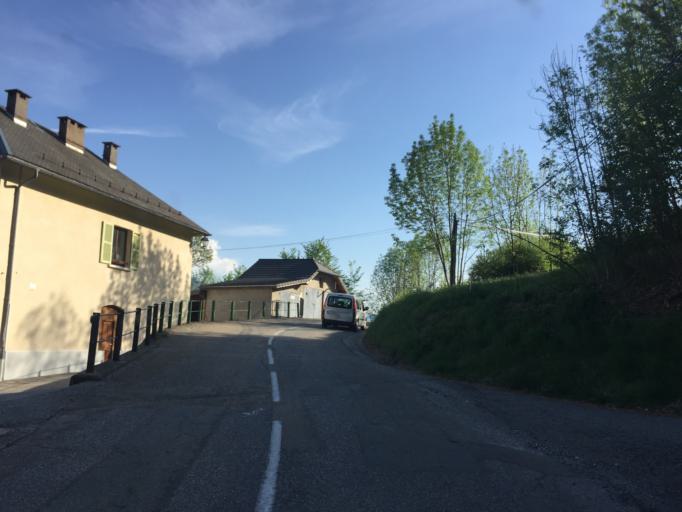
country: FR
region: Rhone-Alpes
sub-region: Departement de la Savoie
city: Mercury
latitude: 45.6652
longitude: 6.3157
